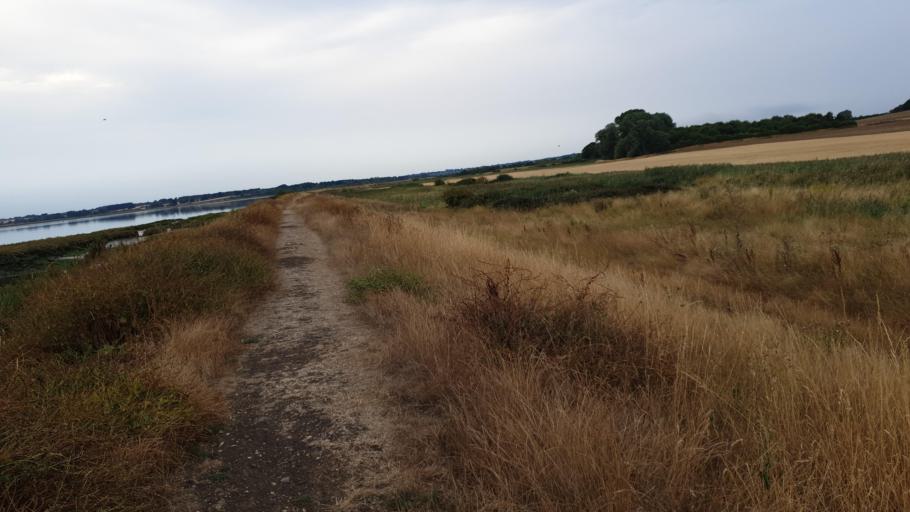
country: GB
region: England
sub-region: Essex
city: Brightlingsea
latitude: 51.8185
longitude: 0.9934
